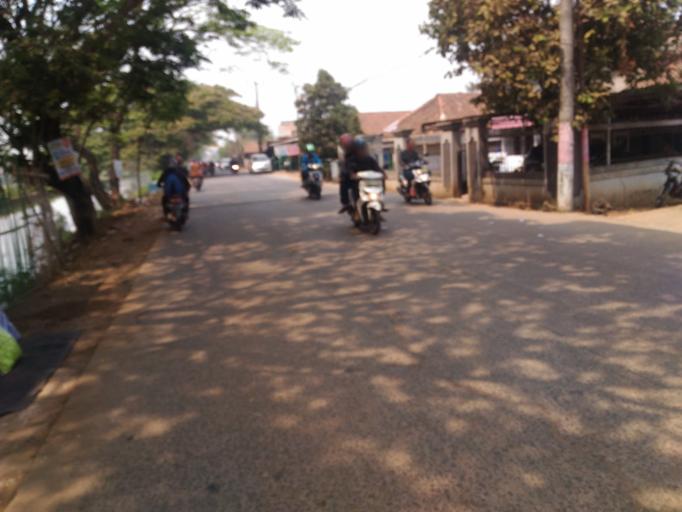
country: ID
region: West Java
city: Pasarkemis
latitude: -6.1417
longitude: 106.5473
